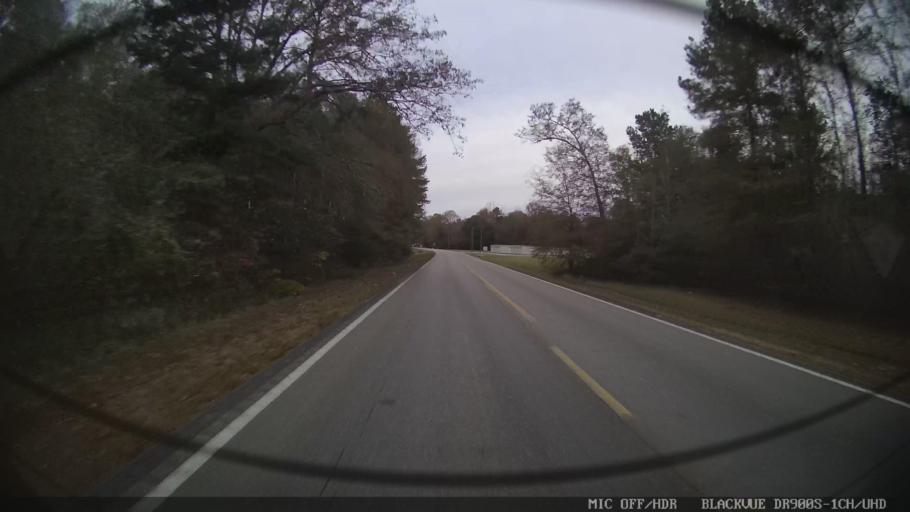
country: US
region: Mississippi
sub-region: Clarke County
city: Stonewall
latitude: 32.0380
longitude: -88.8786
